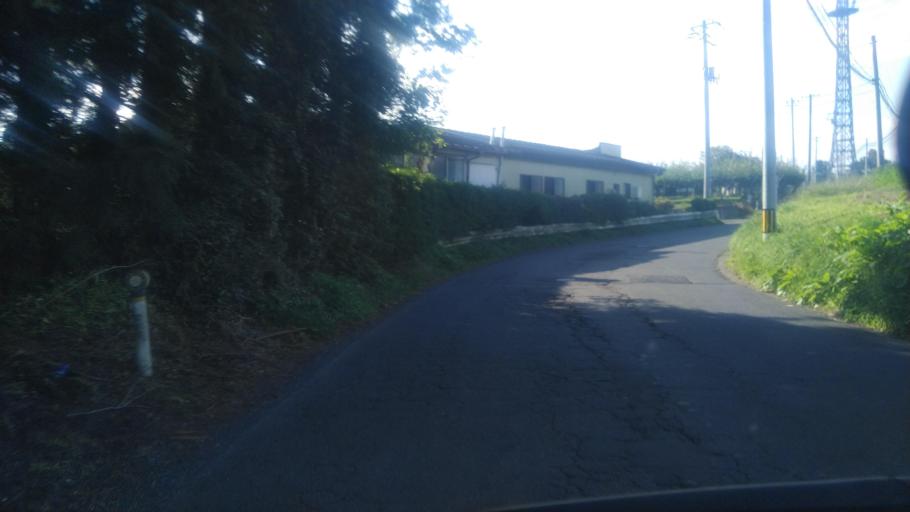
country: JP
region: Miyagi
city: Okawara
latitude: 38.0939
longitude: 140.6682
